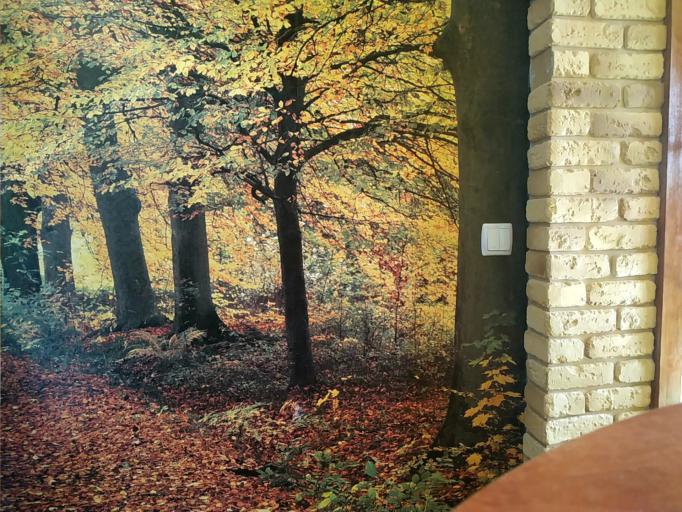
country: RU
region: Jaroslavl
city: Kukoboy
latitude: 58.8627
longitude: 39.7271
